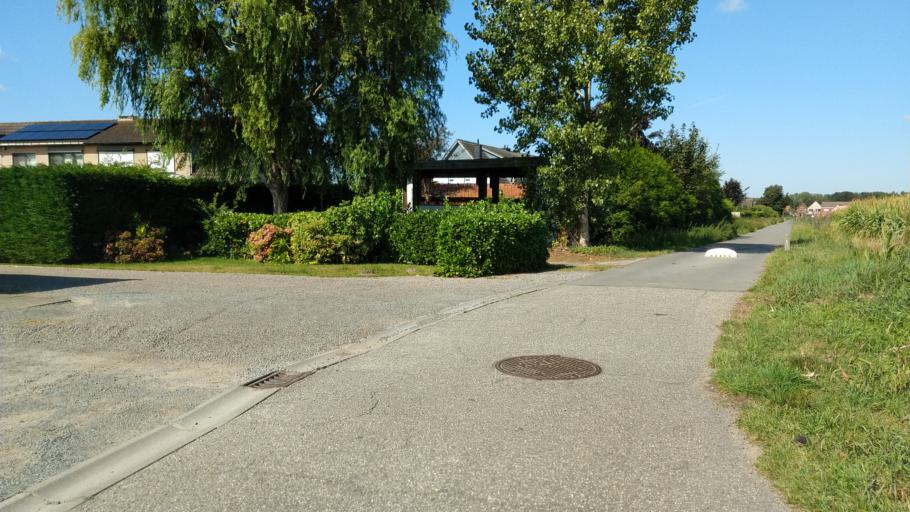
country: BE
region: Flanders
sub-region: Provincie Oost-Vlaanderen
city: Zelzate
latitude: 51.2035
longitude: 3.7973
